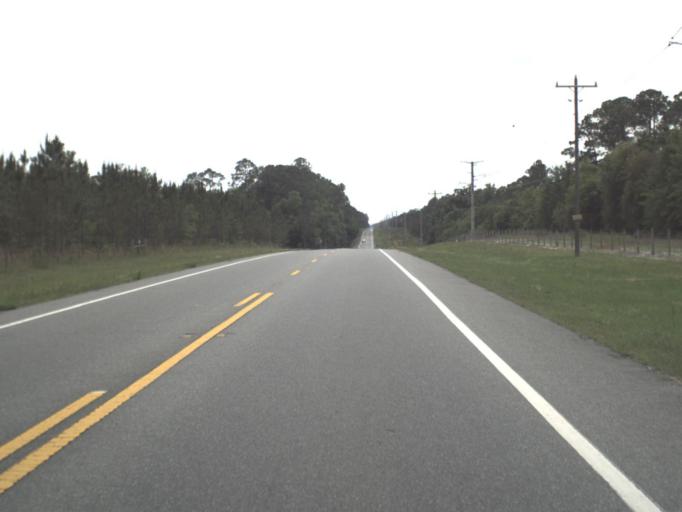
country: US
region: Florida
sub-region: Clay County
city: Middleburg
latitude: 29.9730
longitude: -81.8977
